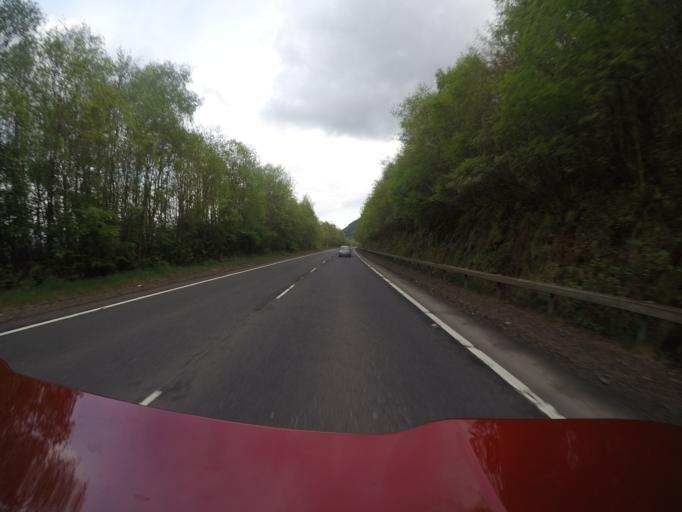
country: GB
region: Scotland
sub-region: Argyll and Bute
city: Helensburgh
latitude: 56.1302
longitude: -4.6553
